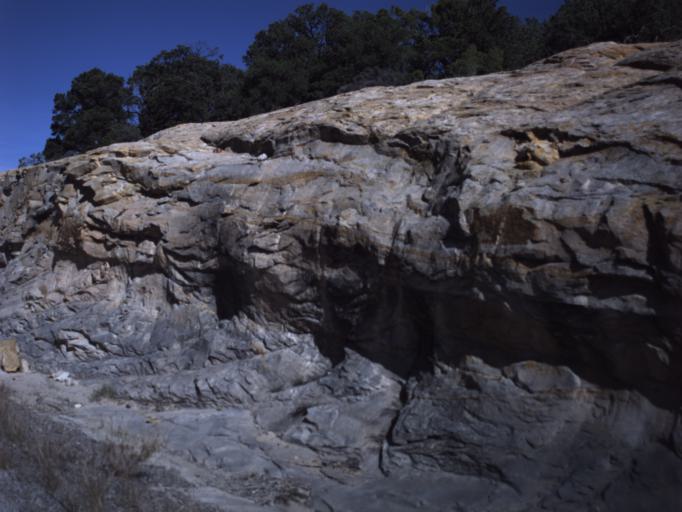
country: US
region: Utah
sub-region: San Juan County
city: Monticello
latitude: 37.9904
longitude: -109.4934
